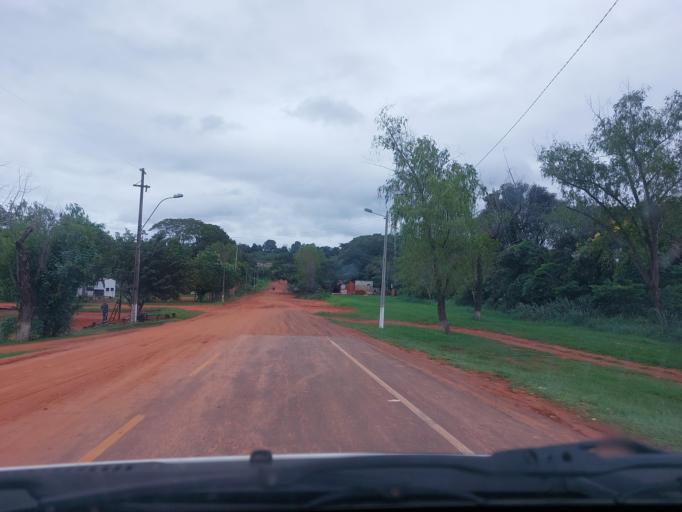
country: PY
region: San Pedro
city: Guayaybi
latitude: -24.6535
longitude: -56.4368
